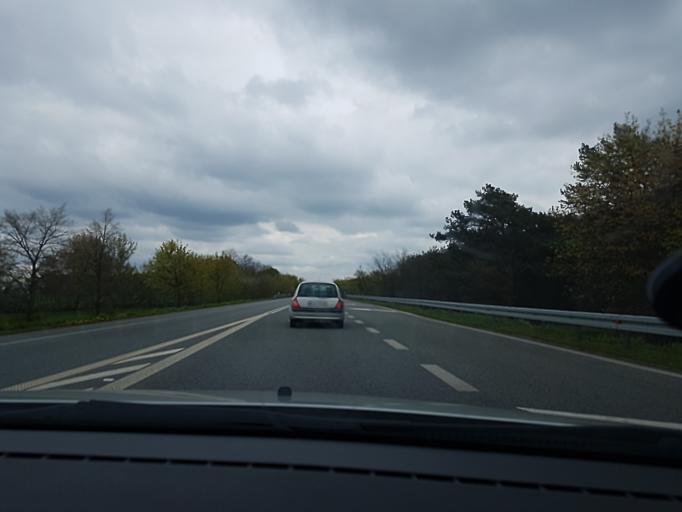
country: PL
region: Lodz Voivodeship
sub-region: powiat Lowicki
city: Lowicz
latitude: 52.1398
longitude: 19.8660
